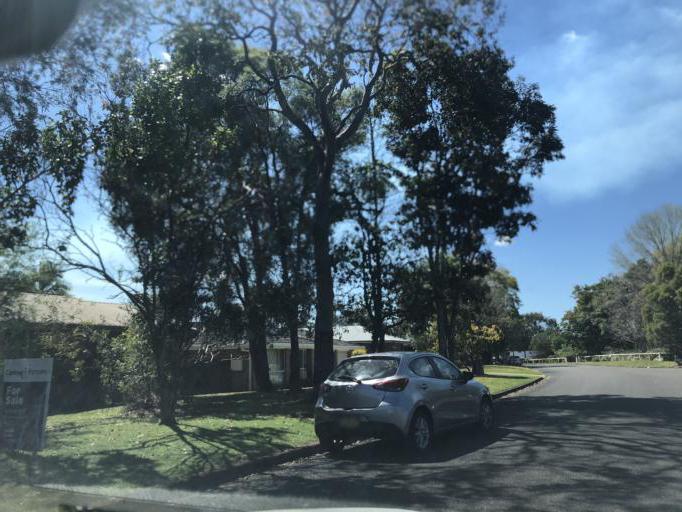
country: AU
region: New South Wales
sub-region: Bellingen
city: Bellingen
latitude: -30.4589
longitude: 152.9046
